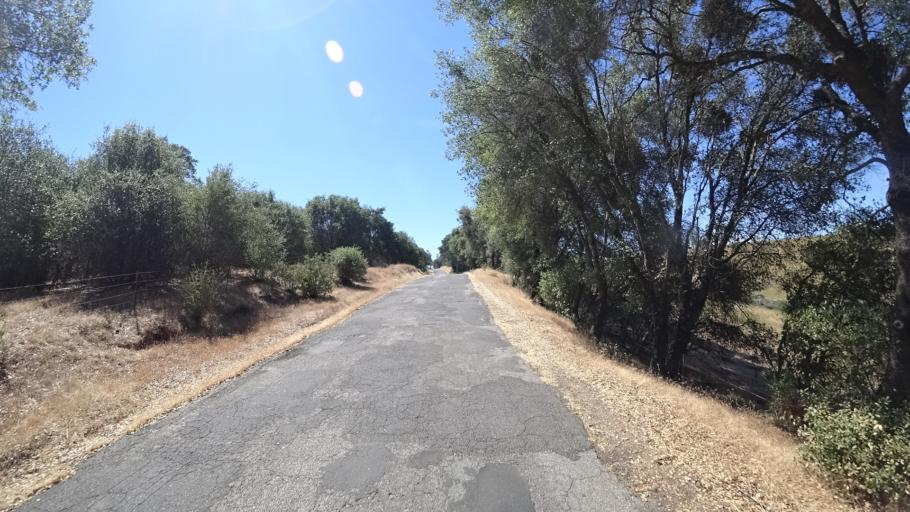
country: US
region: California
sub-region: Calaveras County
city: Angels Camp
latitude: 38.1231
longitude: -120.5745
